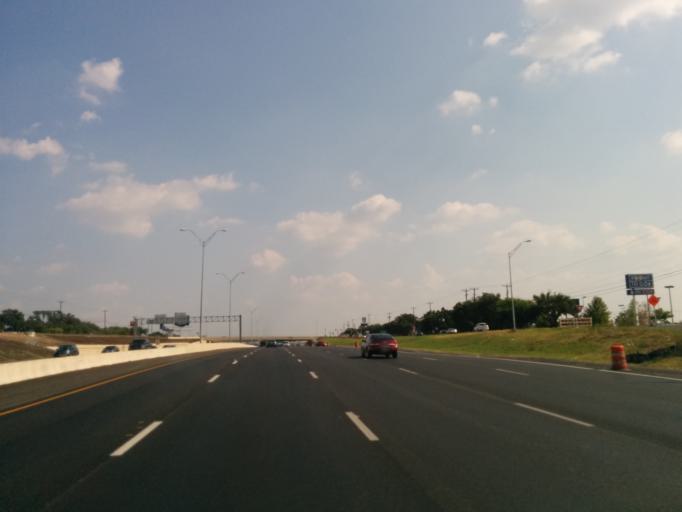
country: US
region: Texas
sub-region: Bexar County
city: Shavano Park
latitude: 29.5821
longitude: -98.5969
